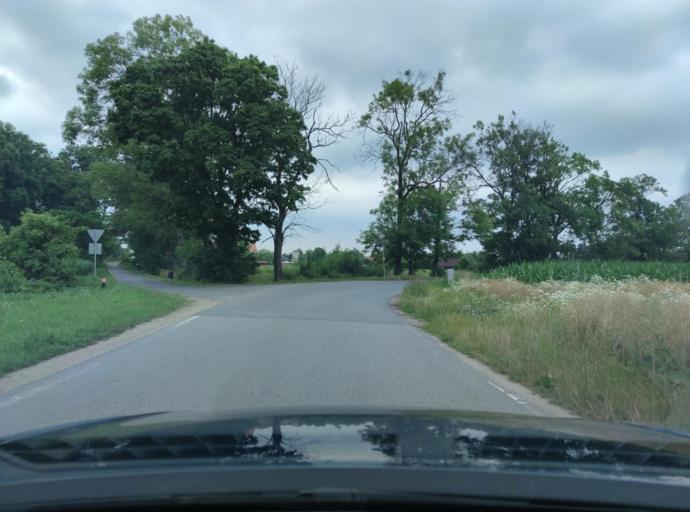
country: PL
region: Lower Silesian Voivodeship
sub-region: Powiat wroclawski
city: Kobierzyce
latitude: 50.9711
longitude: 16.9034
